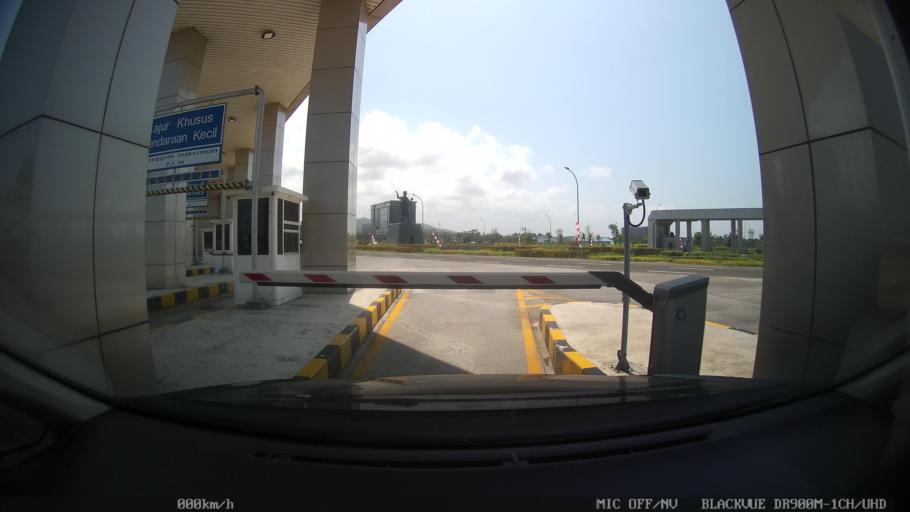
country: ID
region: Daerah Istimewa Yogyakarta
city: Srandakan
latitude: -7.8884
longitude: 110.0628
